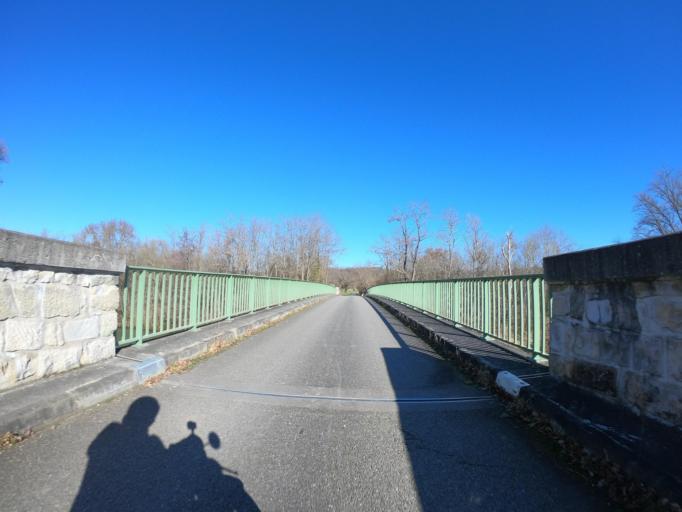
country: FR
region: Midi-Pyrenees
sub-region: Departement de l'Ariege
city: La Tour-du-Crieu
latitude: 43.0979
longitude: 1.7446
